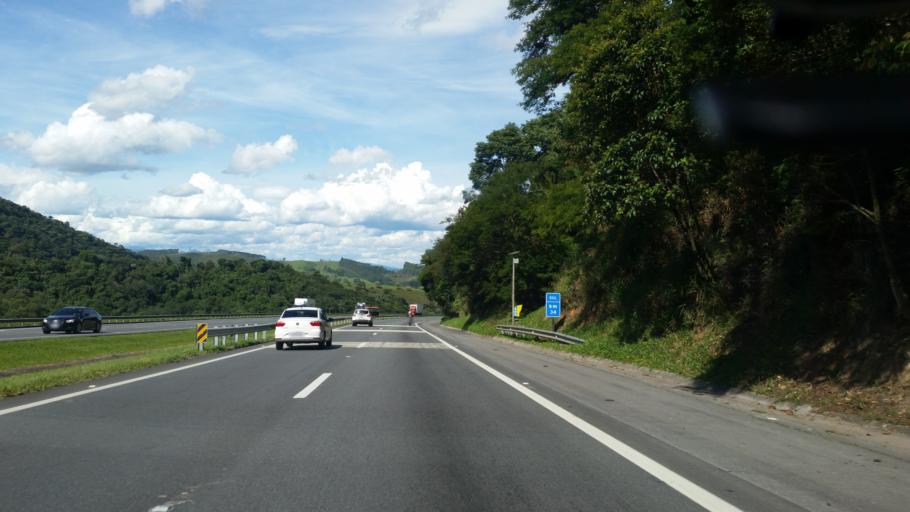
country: BR
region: Sao Paulo
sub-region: Santa Isabel
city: Santa Isabel
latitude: -23.1678
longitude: -46.2394
